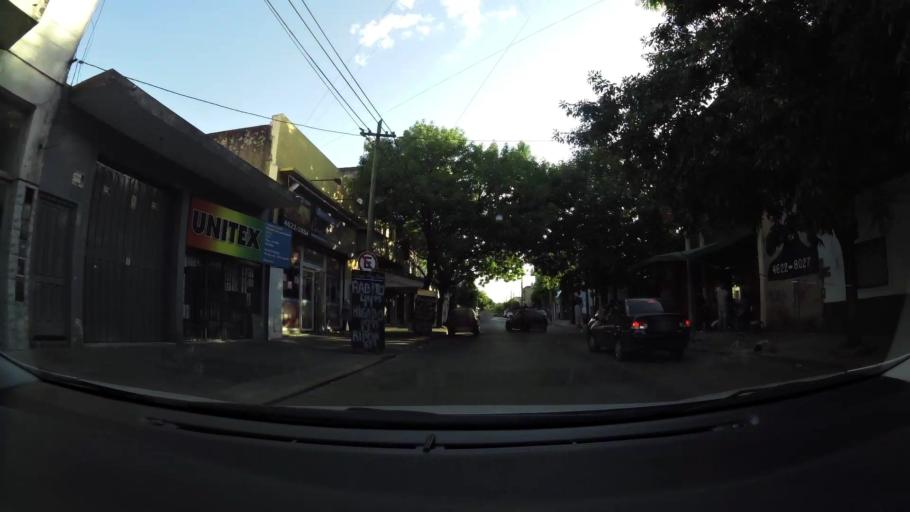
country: AR
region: Buenos Aires F.D.
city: Villa Lugano
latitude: -34.6935
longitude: -58.4841
